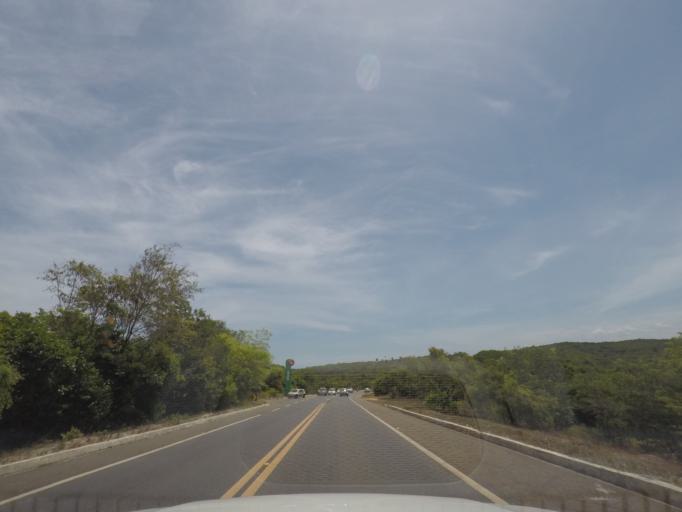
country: BR
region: Bahia
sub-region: Mata De Sao Joao
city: Mata de Sao Joao
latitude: -12.4614
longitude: -37.9538
